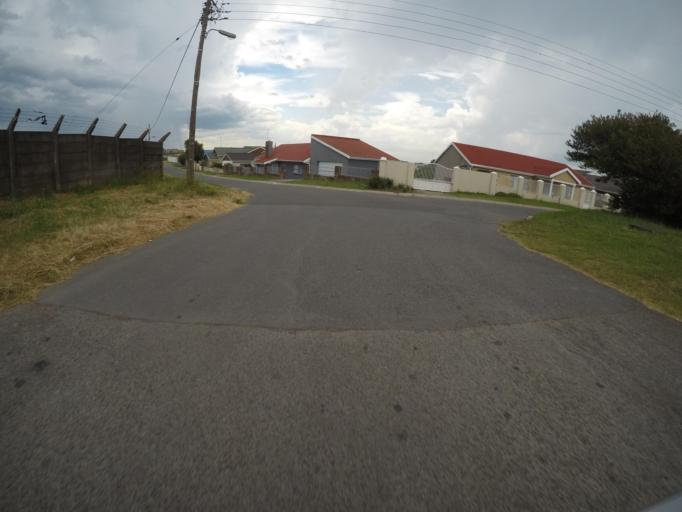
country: ZA
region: Eastern Cape
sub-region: Buffalo City Metropolitan Municipality
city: East London
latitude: -33.0239
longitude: 27.8640
